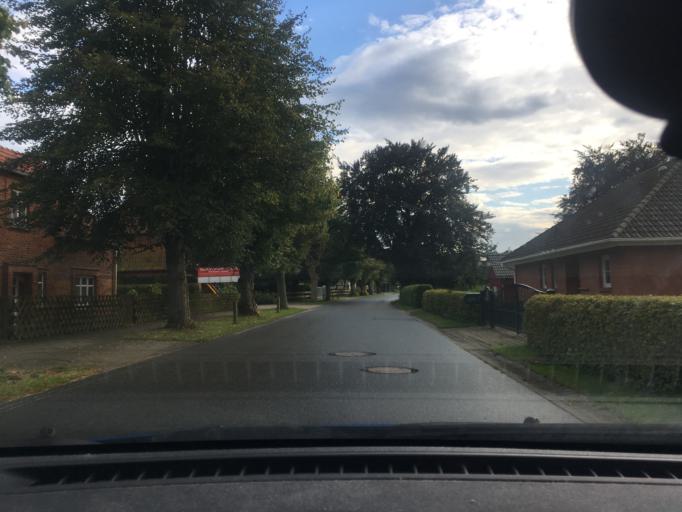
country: DE
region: Lower Saxony
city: Neu Darchau
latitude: 53.2890
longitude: 10.9301
